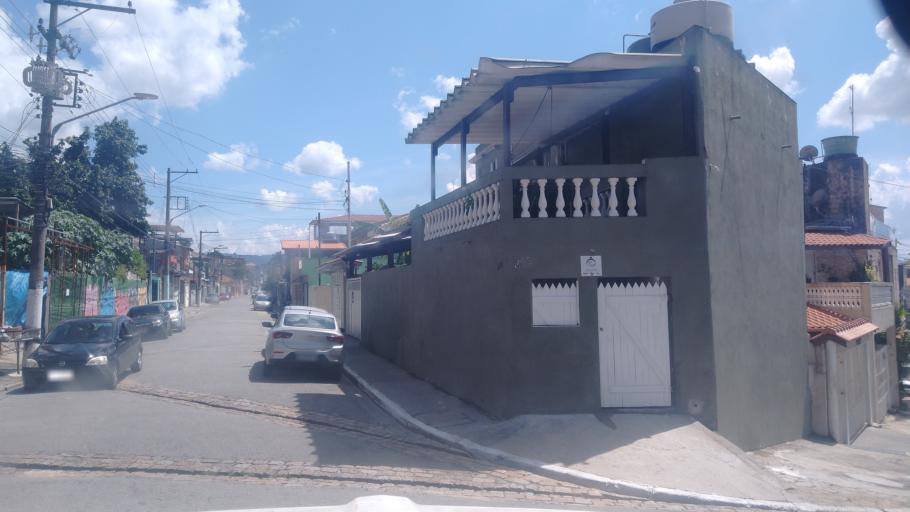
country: BR
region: Sao Paulo
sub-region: Guarulhos
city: Guarulhos
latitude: -23.4832
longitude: -46.5807
